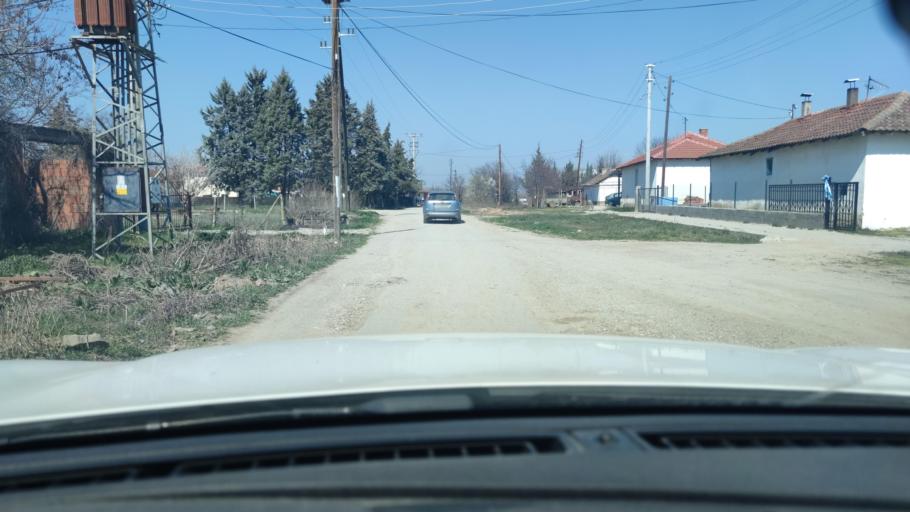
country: MK
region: Rosoman
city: Rosoman
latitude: 41.4748
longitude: 21.9188
